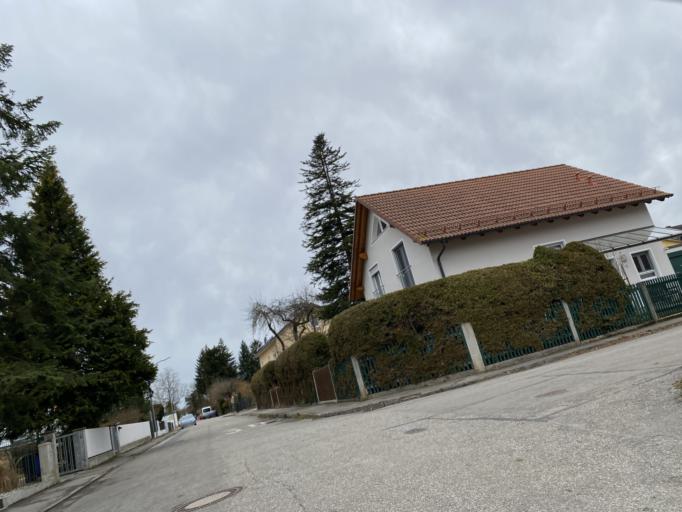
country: DE
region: Bavaria
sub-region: Upper Bavaria
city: Schongeising
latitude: 48.1590
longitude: 11.2282
